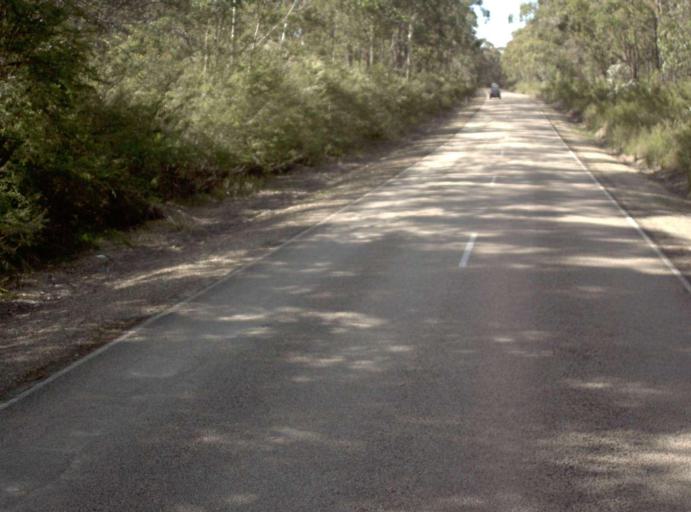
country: AU
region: Victoria
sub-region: East Gippsland
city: Lakes Entrance
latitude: -37.6335
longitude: 148.1104
